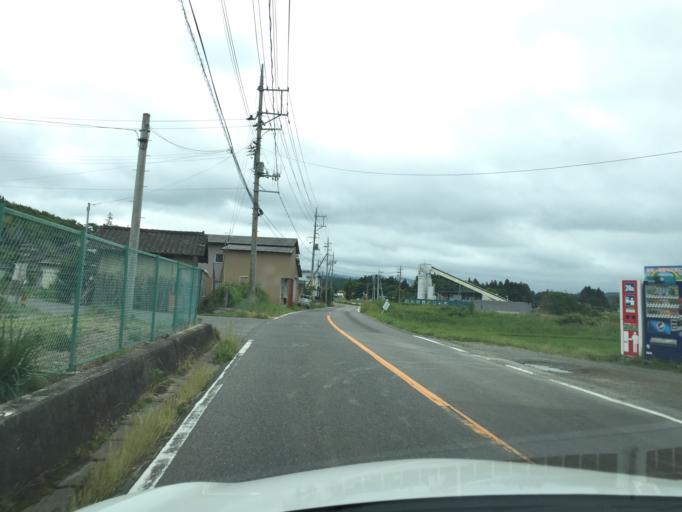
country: JP
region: Fukushima
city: Funehikimachi-funehiki
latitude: 37.4285
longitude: 140.5952
